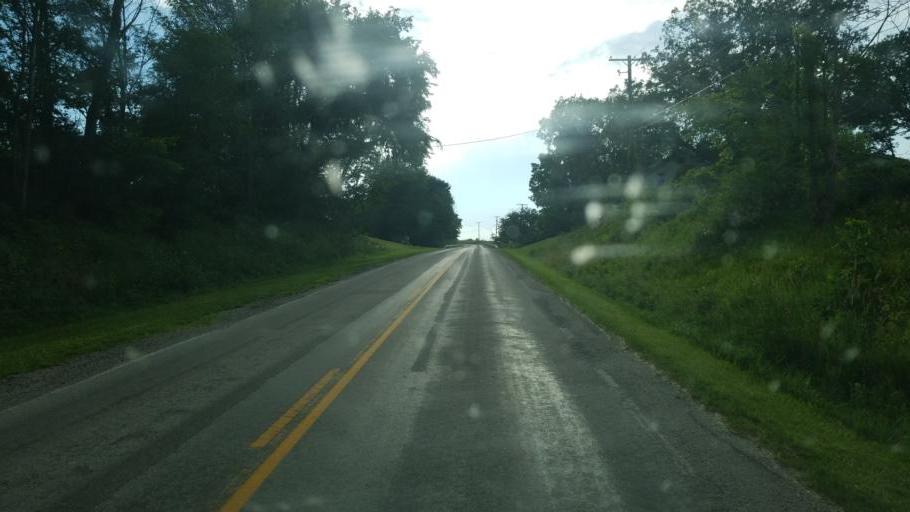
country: US
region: Ohio
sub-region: Ashland County
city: Ashland
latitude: 40.7729
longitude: -82.2916
